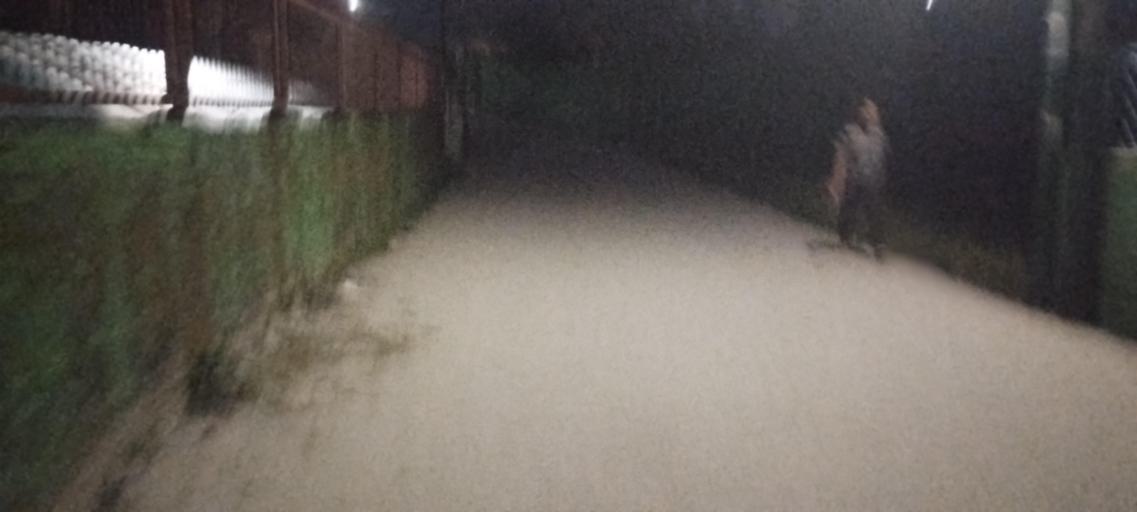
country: NP
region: Central Region
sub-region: Bagmati Zone
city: Kathmandu
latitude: 27.7706
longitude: 85.3608
